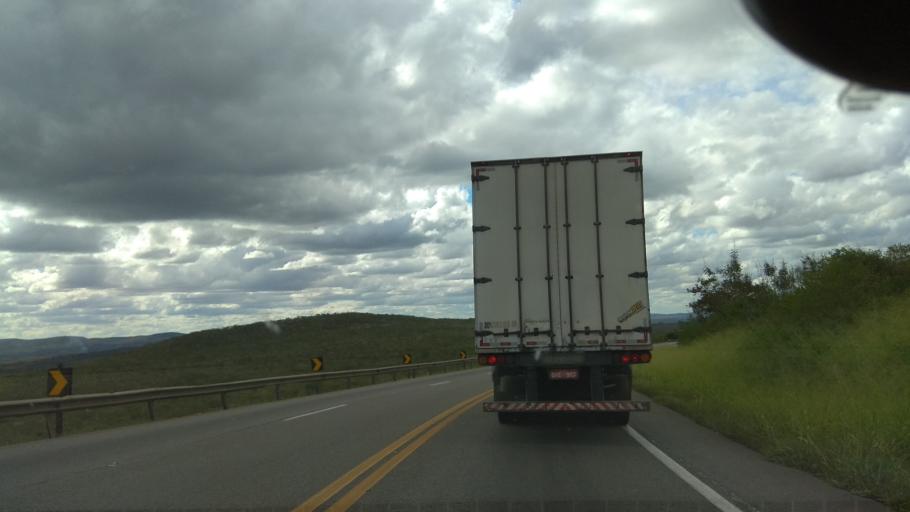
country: BR
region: Bahia
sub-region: Santa Ines
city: Santa Ines
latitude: -13.0385
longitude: -39.9680
